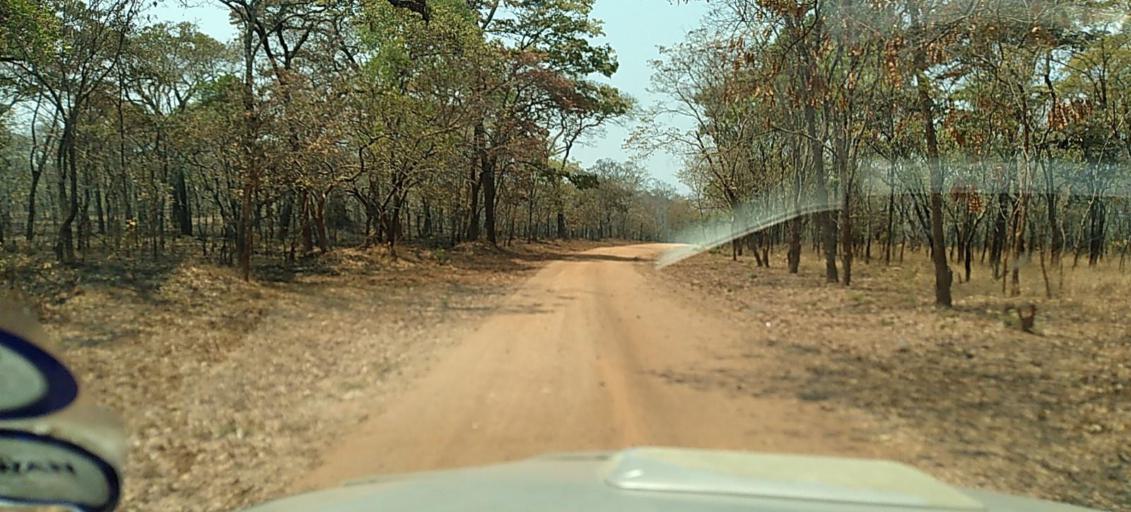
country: ZM
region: North-Western
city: Kasempa
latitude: -13.5564
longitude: 26.0721
